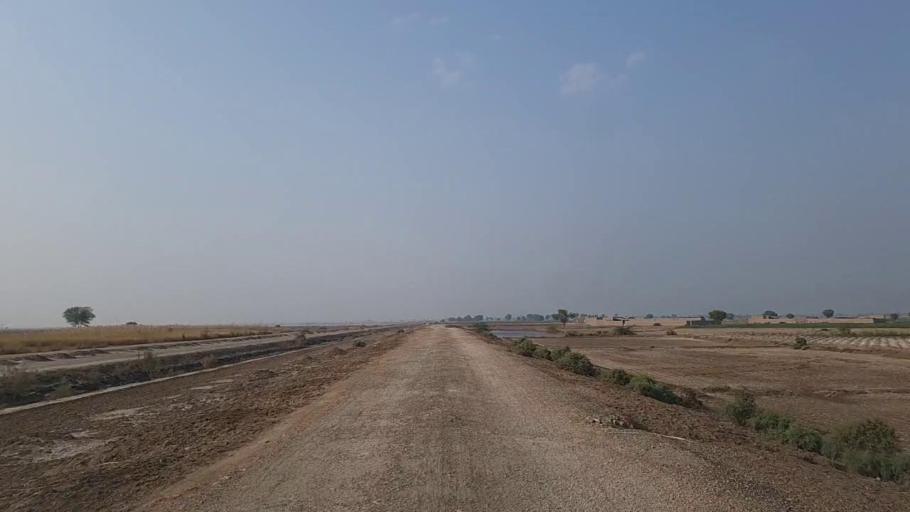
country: PK
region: Sindh
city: Nawabshah
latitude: 26.3323
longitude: 68.4751
